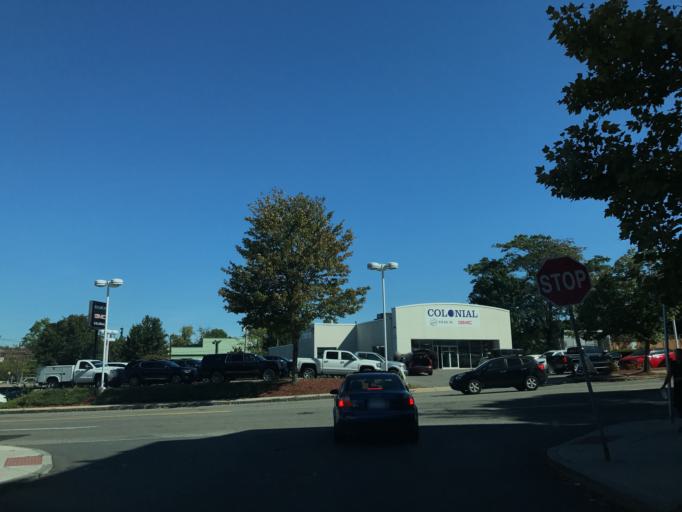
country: US
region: Massachusetts
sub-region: Middlesex County
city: Watertown
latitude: 42.3633
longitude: -71.1864
